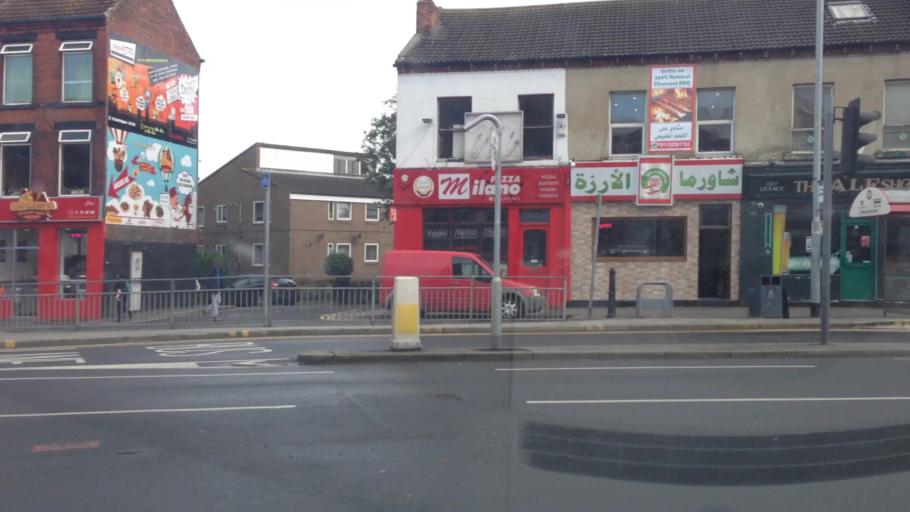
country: GB
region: England
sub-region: City and Borough of Leeds
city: Leeds
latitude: 53.8107
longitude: -1.5564
